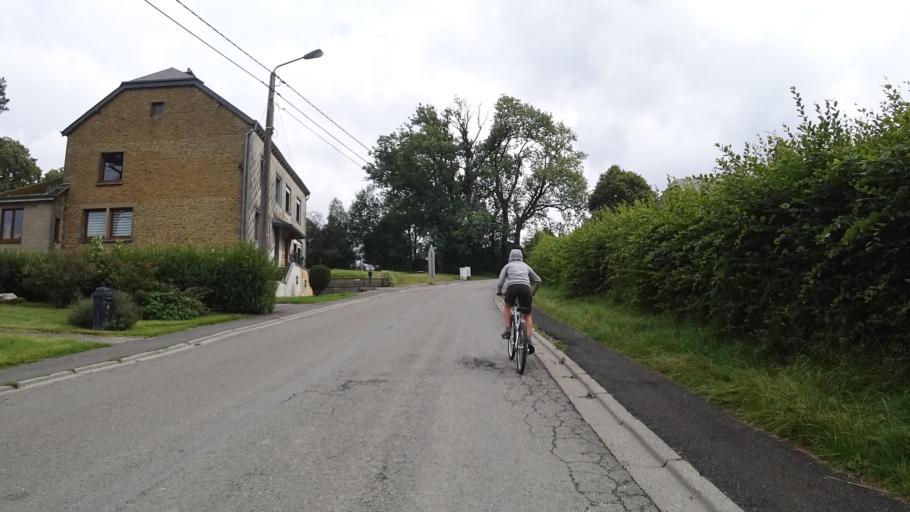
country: BE
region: Wallonia
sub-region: Province du Luxembourg
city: Chiny
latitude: 49.8177
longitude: 5.3282
